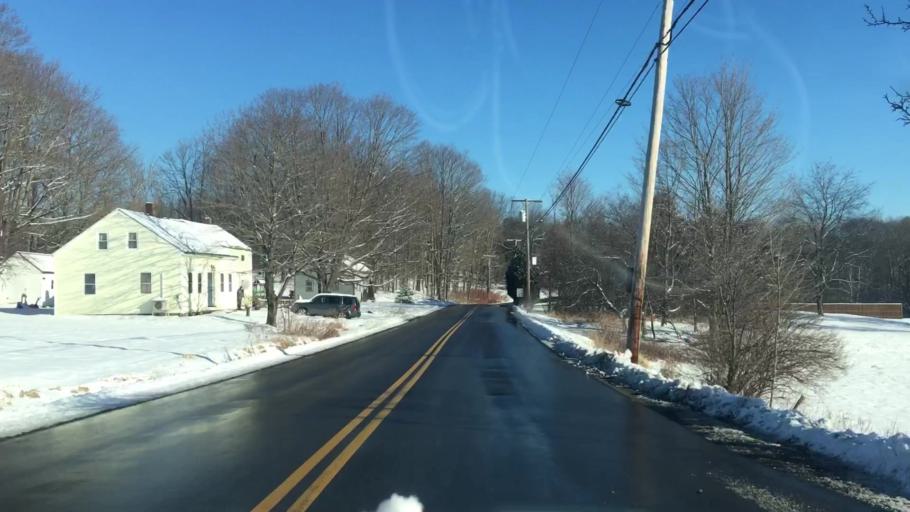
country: US
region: Maine
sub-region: Androscoggin County
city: Lisbon
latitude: 43.9492
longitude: -70.1467
